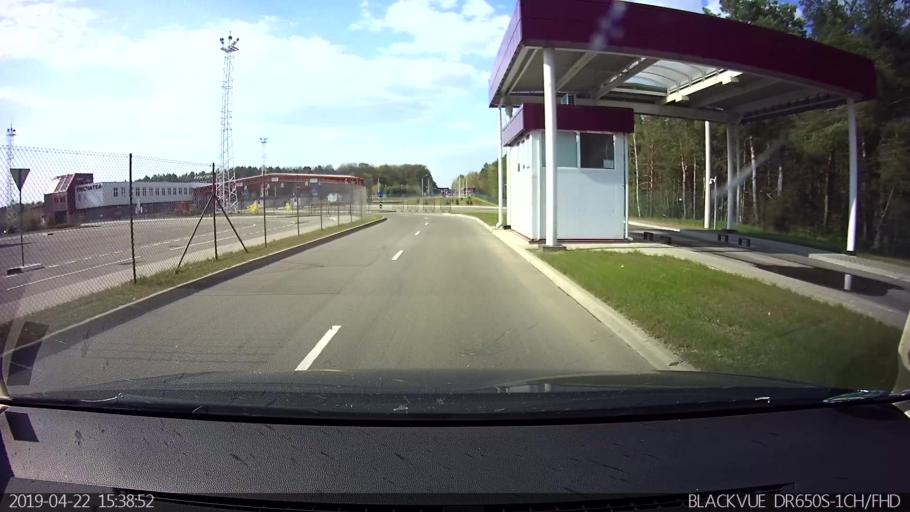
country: PL
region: Podlasie
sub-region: Powiat hajnowski
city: Czeremcha
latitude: 52.4655
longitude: 23.3609
